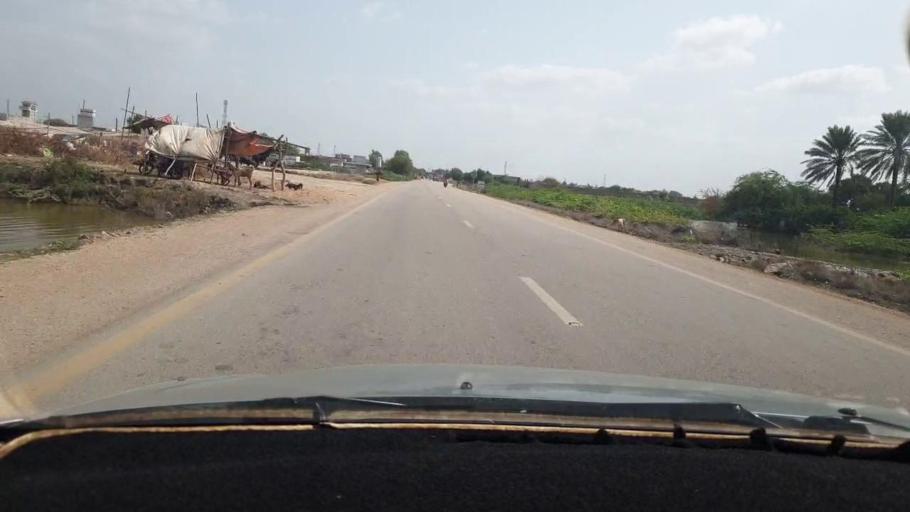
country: PK
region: Sindh
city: Naukot
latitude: 24.9808
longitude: 69.2940
